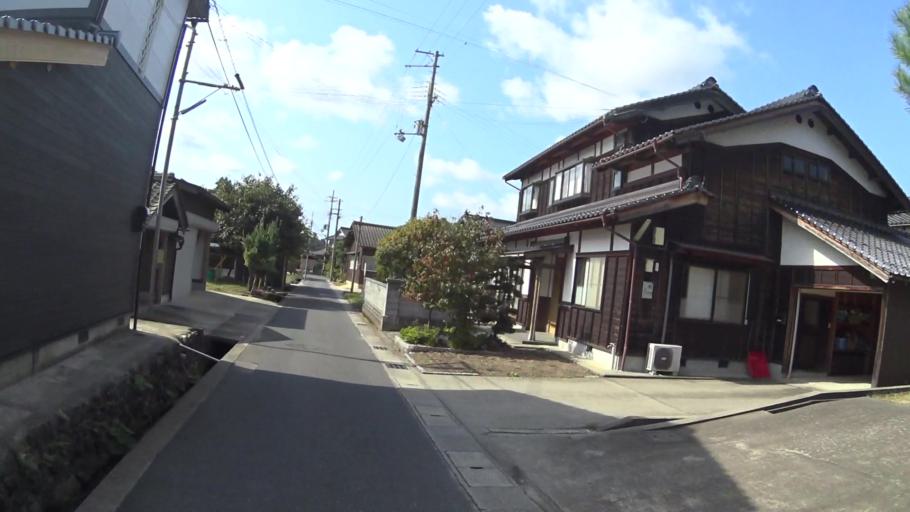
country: JP
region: Kyoto
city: Miyazu
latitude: 35.6565
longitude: 135.1117
